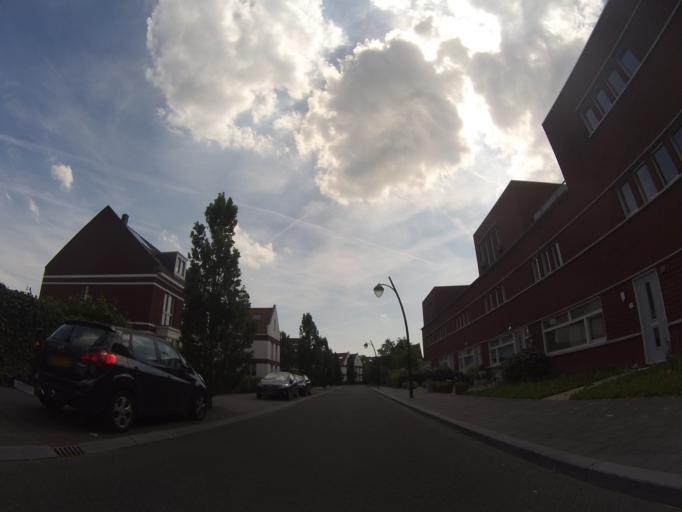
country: NL
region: Utrecht
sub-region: Gemeente Amersfoort
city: Randenbroek
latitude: 52.1899
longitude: 5.4218
